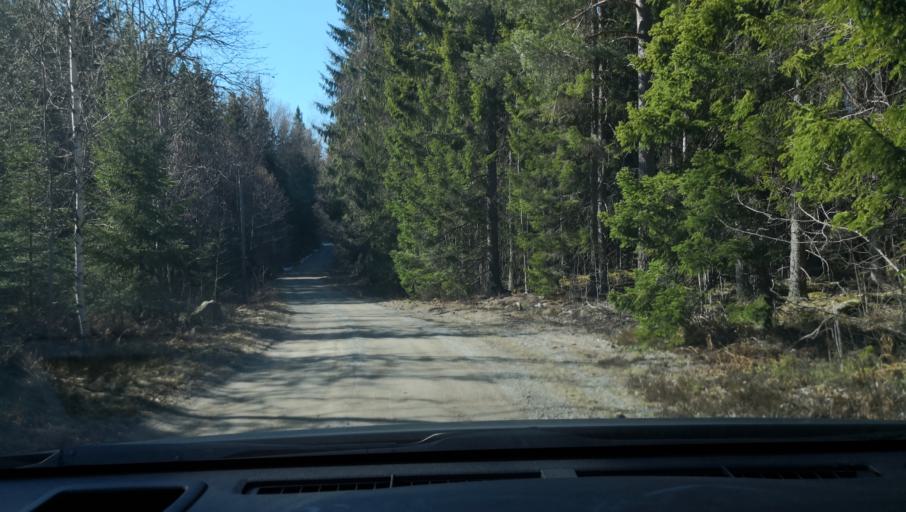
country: SE
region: Vaestmanland
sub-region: Sala Kommun
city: Sala
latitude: 59.9410
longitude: 16.4450
